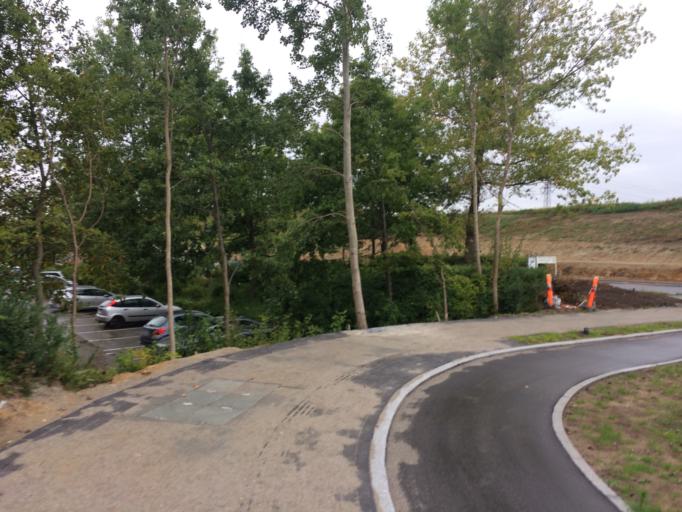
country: DK
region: Central Jutland
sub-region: Arhus Kommune
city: Stavtrup
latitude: 56.1641
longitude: 10.1404
